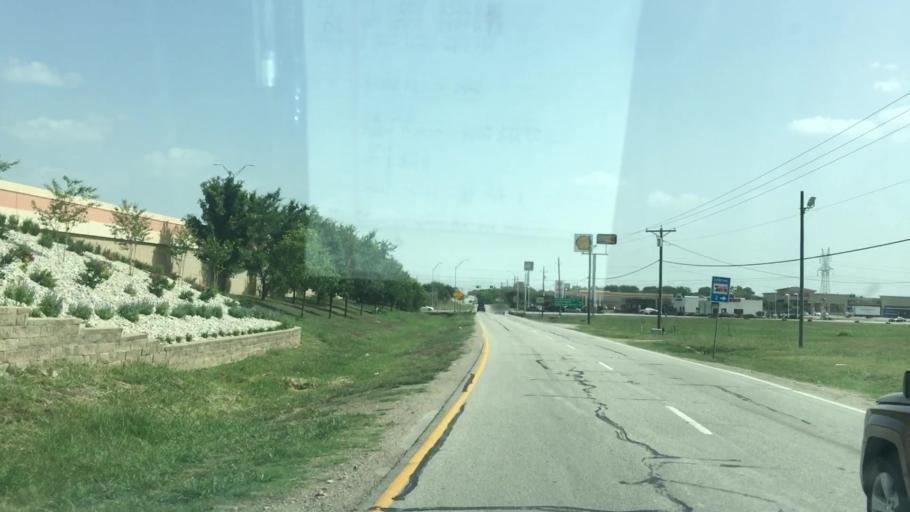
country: US
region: Texas
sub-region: Dallas County
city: Glenn Heights
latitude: 32.5628
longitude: -96.8229
